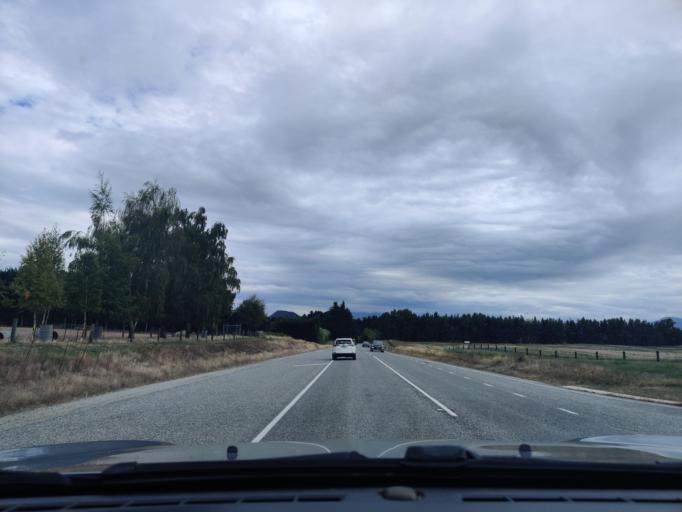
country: NZ
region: Otago
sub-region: Queenstown-Lakes District
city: Wanaka
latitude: -44.7155
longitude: 169.2135
